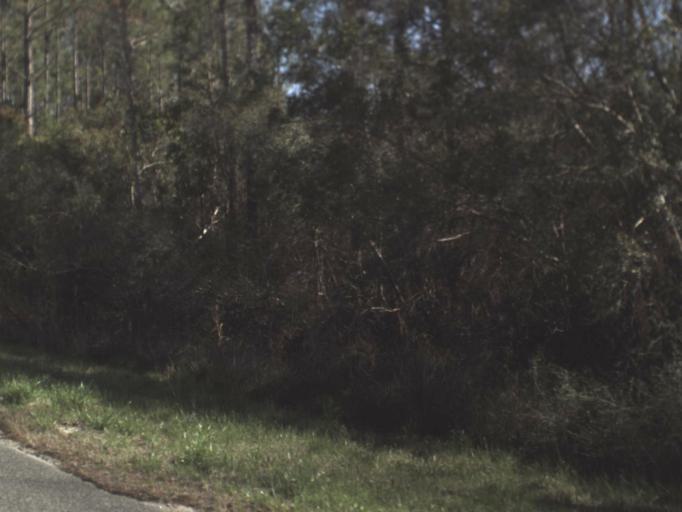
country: US
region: Florida
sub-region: Leon County
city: Woodville
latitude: 30.2991
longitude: -84.0480
